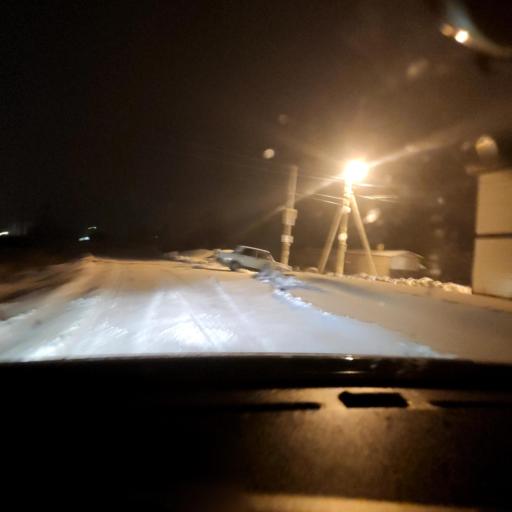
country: RU
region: Bashkortostan
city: Kabakovo
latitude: 54.6837
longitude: 56.1434
